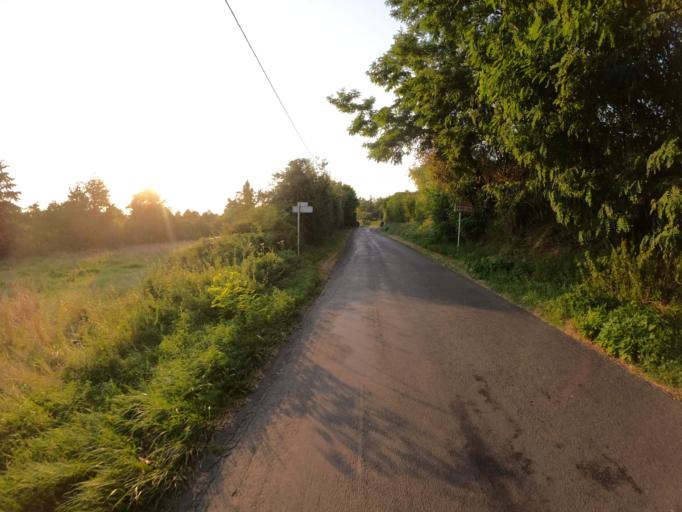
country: FR
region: Pays de la Loire
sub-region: Departement de la Sarthe
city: Parce-sur-Sarthe
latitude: 47.8609
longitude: -0.1980
